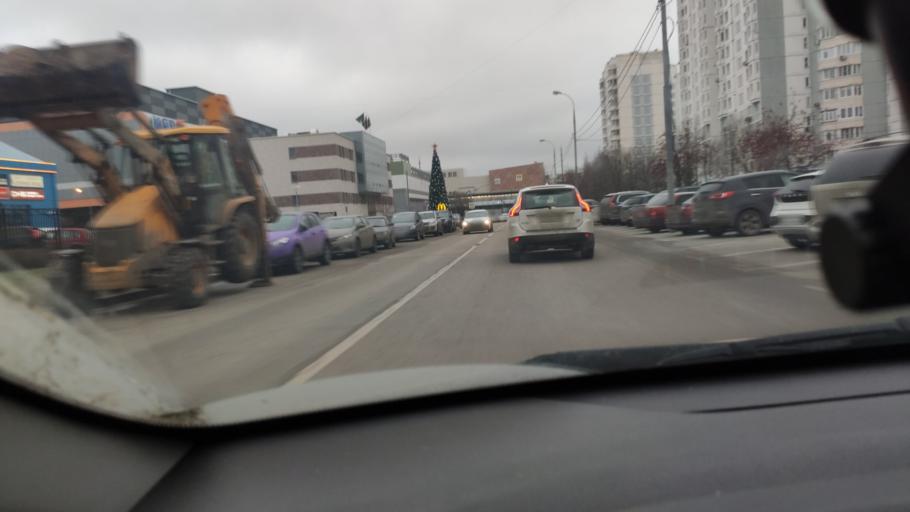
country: RU
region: Moskovskaya
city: Shcherbinka
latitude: 55.5486
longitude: 37.5409
